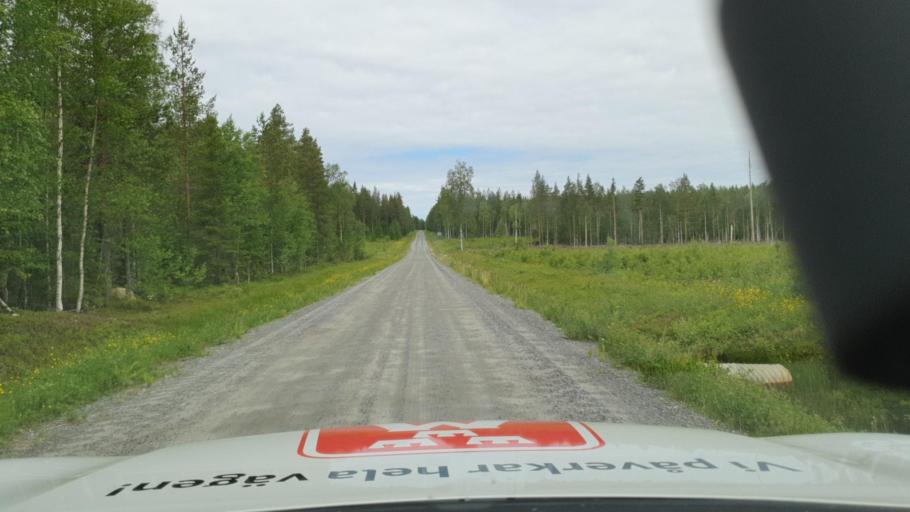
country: SE
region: Vaesterbotten
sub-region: Skelleftea Kommun
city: Burtraesk
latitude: 64.4530
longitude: 20.2943
